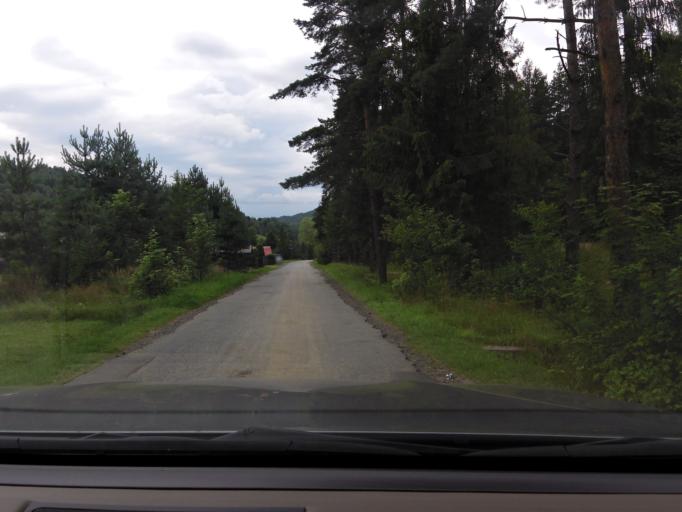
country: PL
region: Silesian Voivodeship
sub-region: Powiat zywiecki
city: Rajcza
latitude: 49.5018
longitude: 19.1236
